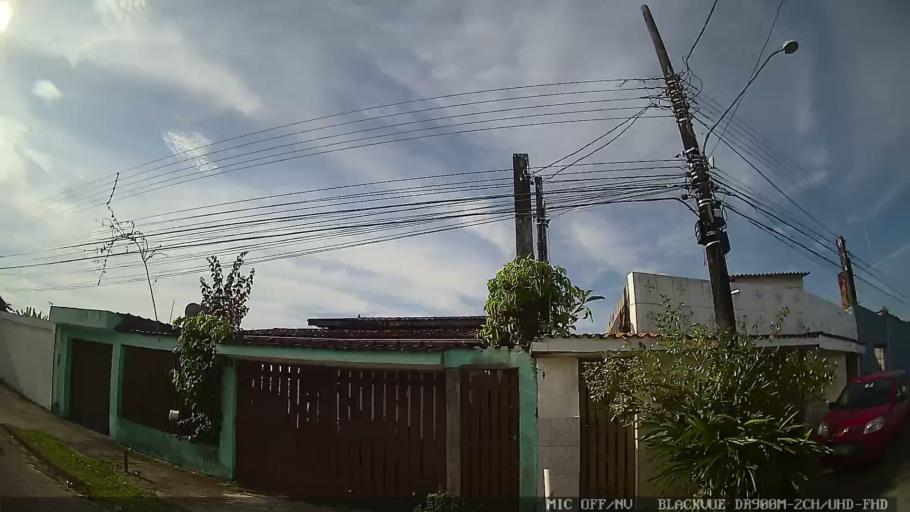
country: BR
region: Sao Paulo
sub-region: Itanhaem
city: Itanhaem
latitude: -24.1658
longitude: -46.7651
